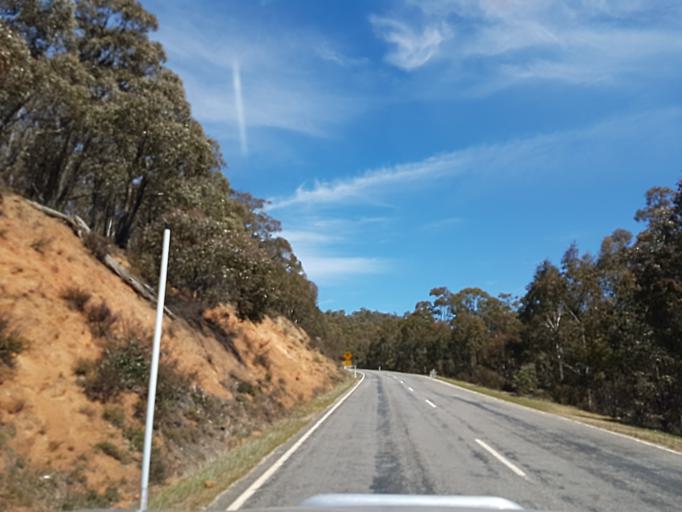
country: AU
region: Victoria
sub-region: Alpine
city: Mount Beauty
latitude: -37.0822
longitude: 147.3789
